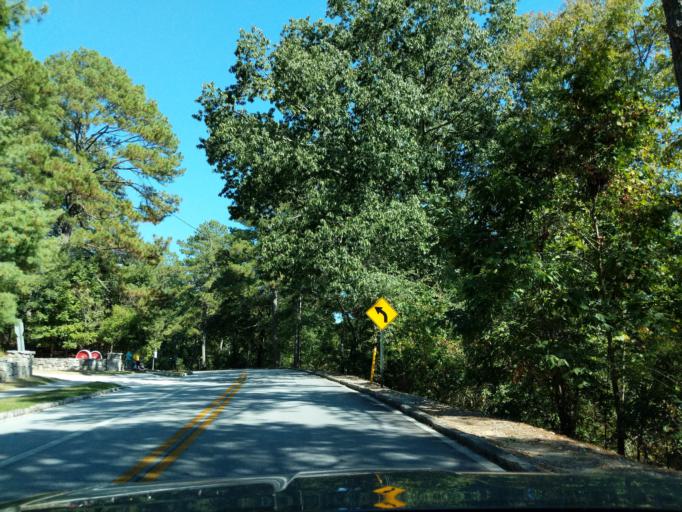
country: US
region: Georgia
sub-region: DeKalb County
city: Stone Mountain
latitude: 33.7989
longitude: -84.1358
